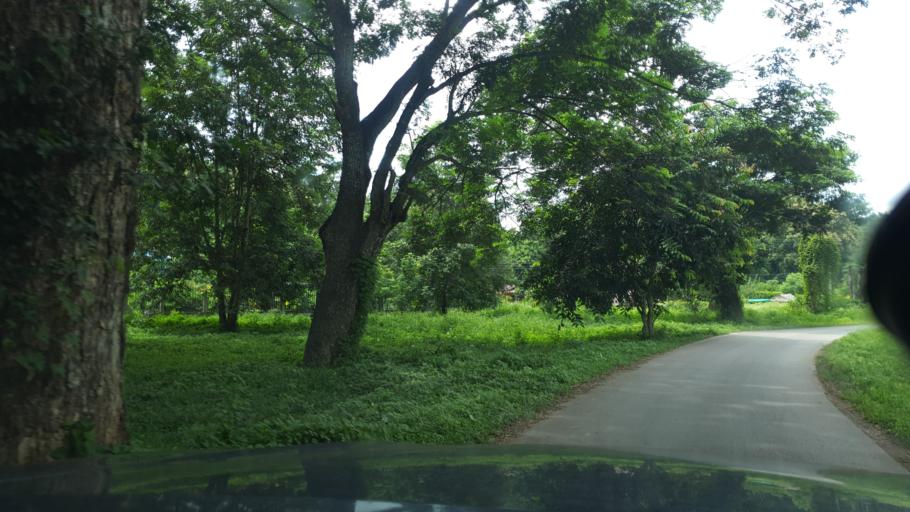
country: TH
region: Lampang
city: Hang Chat
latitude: 18.4044
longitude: 99.2617
